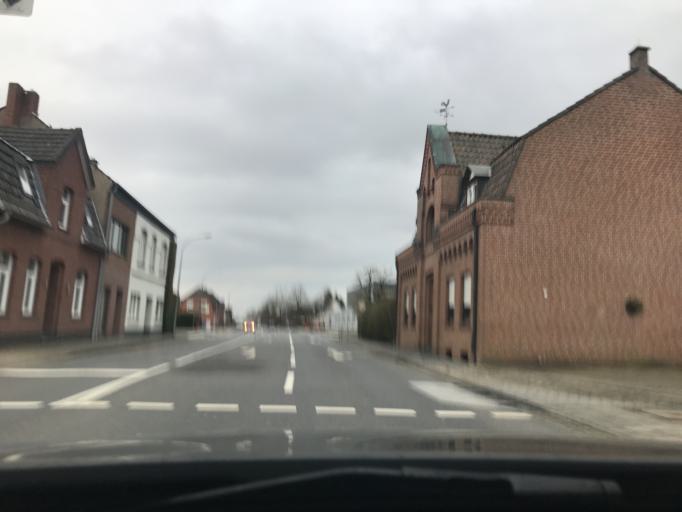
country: DE
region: North Rhine-Westphalia
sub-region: Regierungsbezirk Dusseldorf
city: Uedem
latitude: 51.6650
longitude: 6.2752
